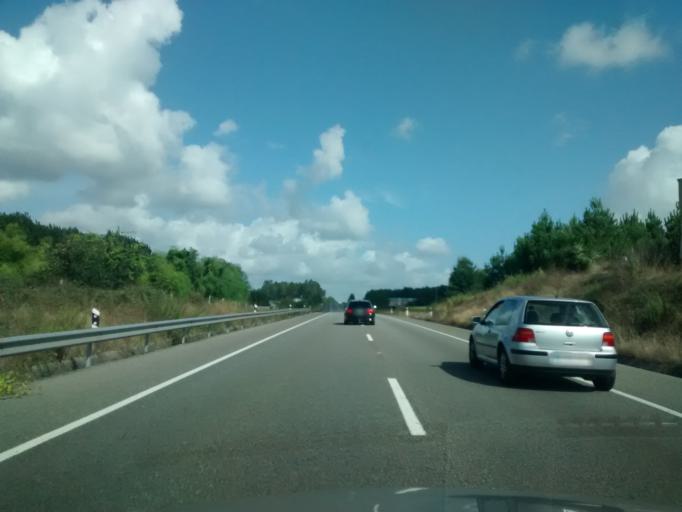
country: PT
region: Aveiro
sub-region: Anadia
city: Sangalhos
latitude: 40.4714
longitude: -8.4697
